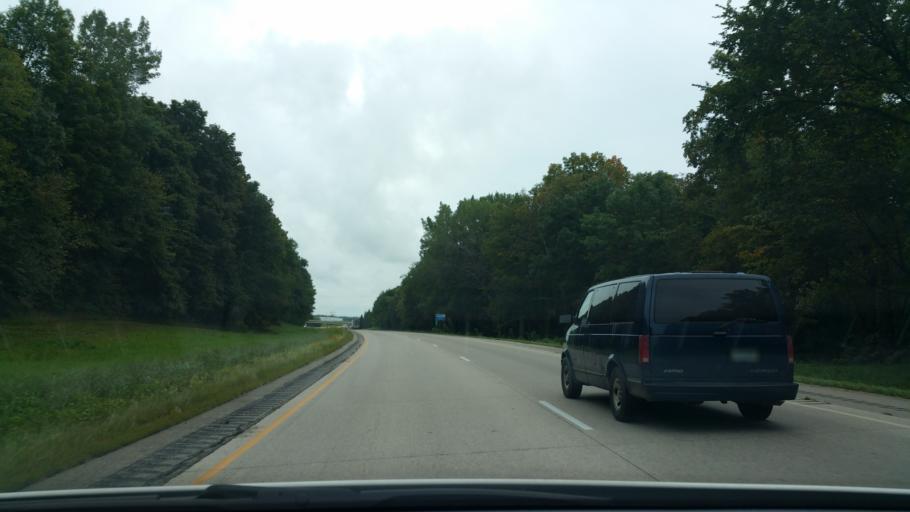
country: US
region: Minnesota
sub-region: Rice County
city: Faribault
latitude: 44.3772
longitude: -93.2954
